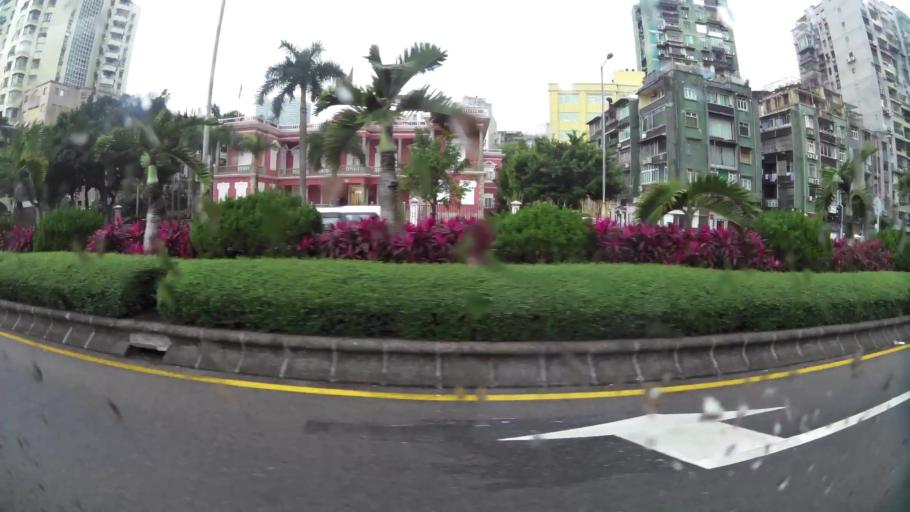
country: MO
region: Macau
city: Macau
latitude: 22.1898
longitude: 113.5385
